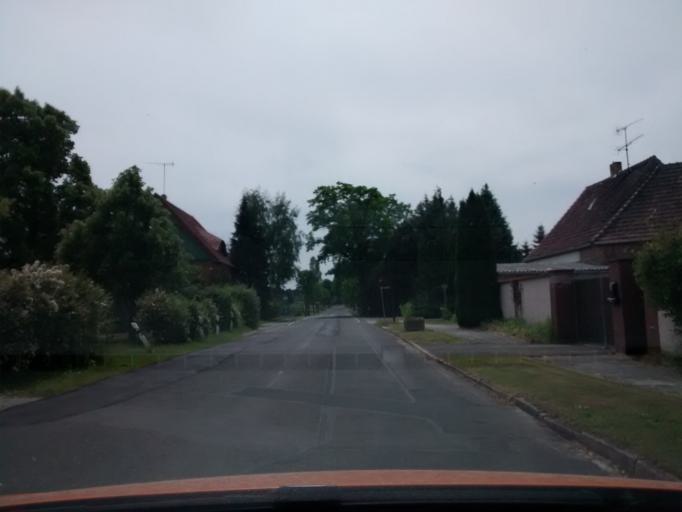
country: DE
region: Saxony-Anhalt
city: Holzdorf
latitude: 51.8368
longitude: 13.2199
